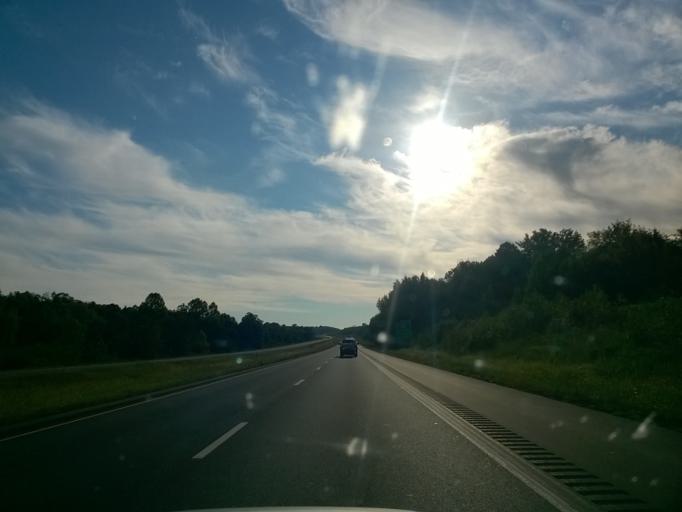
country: US
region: Indiana
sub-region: Warrick County
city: Boonville
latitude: 38.1921
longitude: -87.3101
